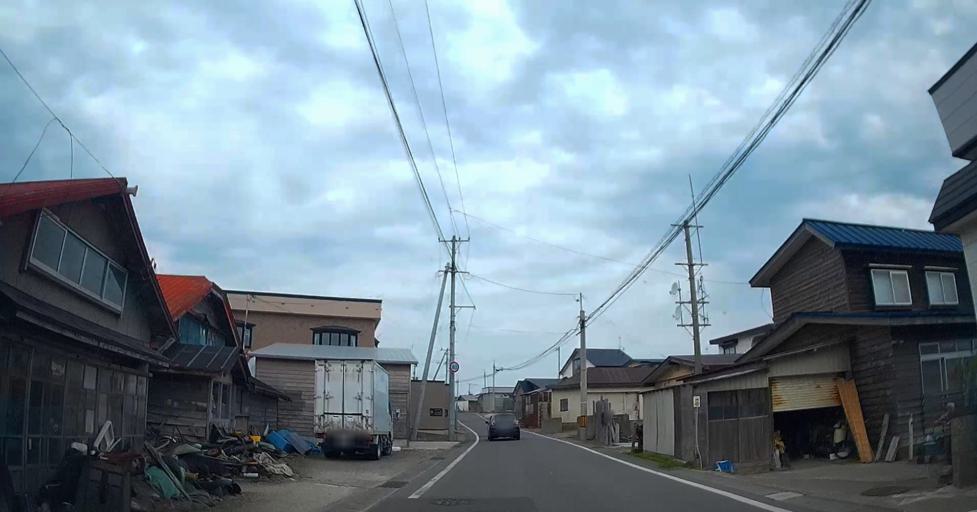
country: JP
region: Aomori
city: Shimokizukuri
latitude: 41.0254
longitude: 140.3276
